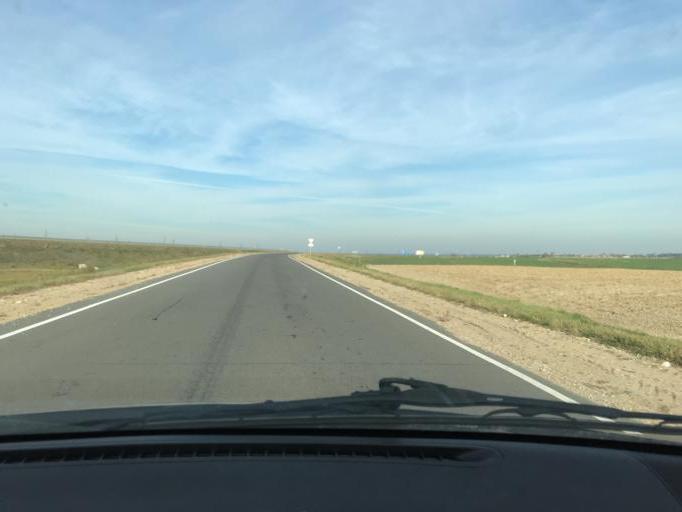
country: BY
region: Brest
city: Asnyezhytsy
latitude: 52.1841
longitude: 26.0837
